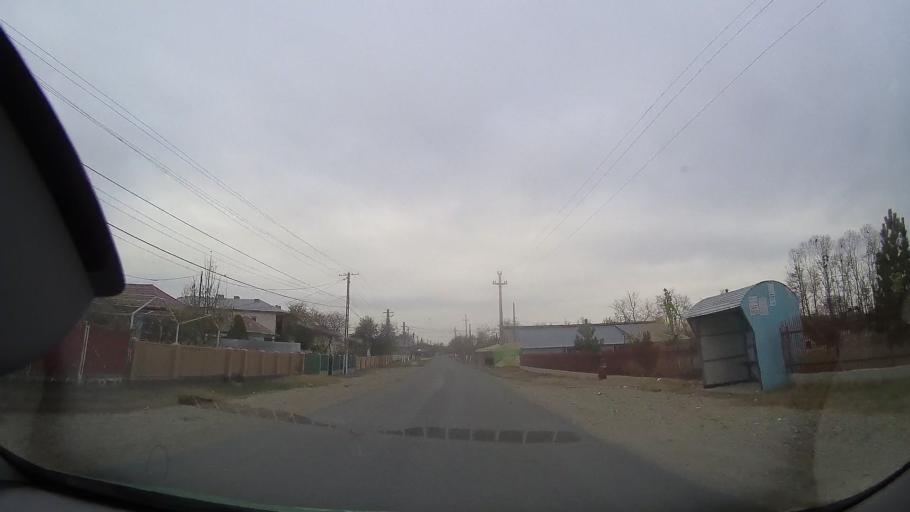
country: RO
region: Buzau
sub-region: Comuna Largu
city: Largu
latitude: 44.9748
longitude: 27.1481
